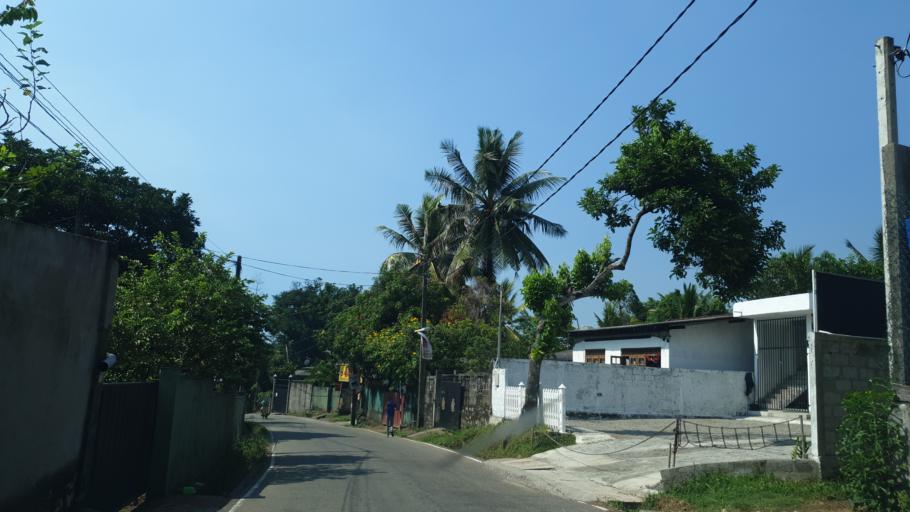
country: LK
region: Western
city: Moratuwa
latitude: 6.7654
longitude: 79.9346
